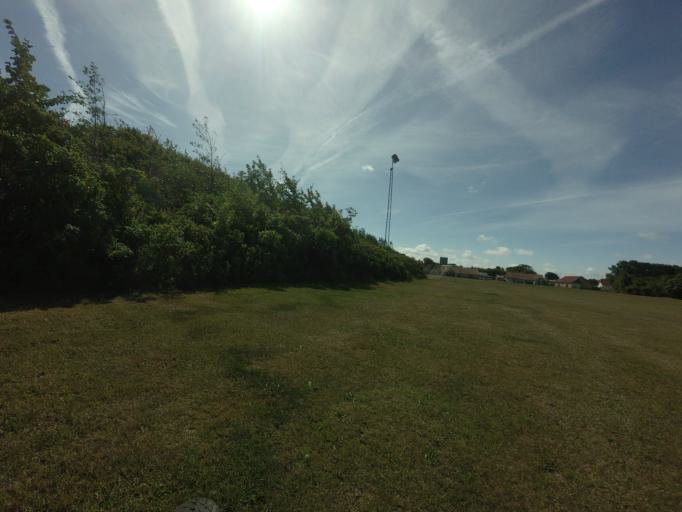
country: DK
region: North Denmark
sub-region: Jammerbugt Kommune
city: Pandrup
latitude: 57.3399
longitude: 9.7727
